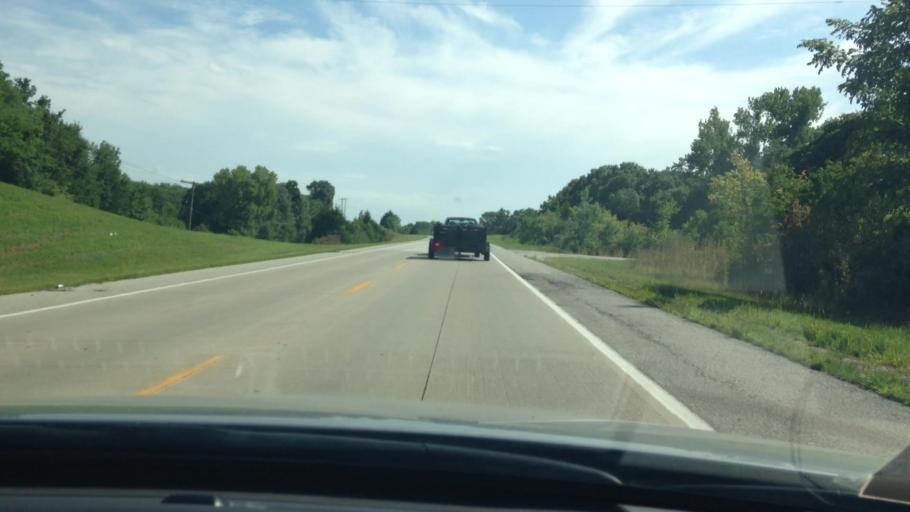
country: US
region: Missouri
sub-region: Jackson County
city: Grandview
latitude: 38.8568
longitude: -94.5860
